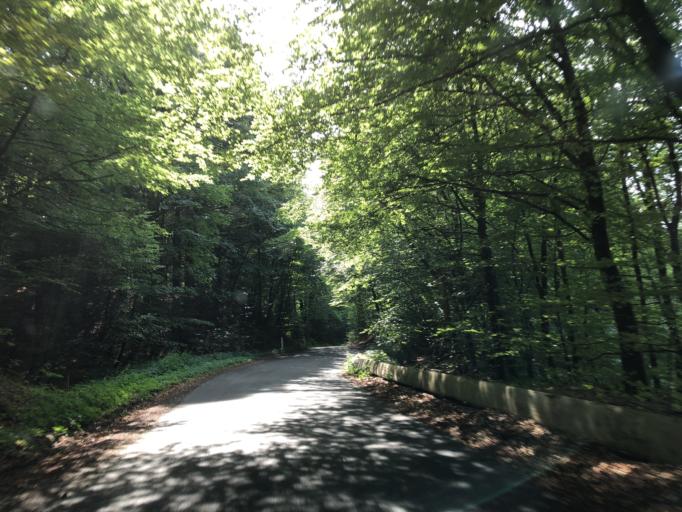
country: DK
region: South Denmark
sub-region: Vejle Kommune
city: Egtved
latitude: 55.6745
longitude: 9.2960
